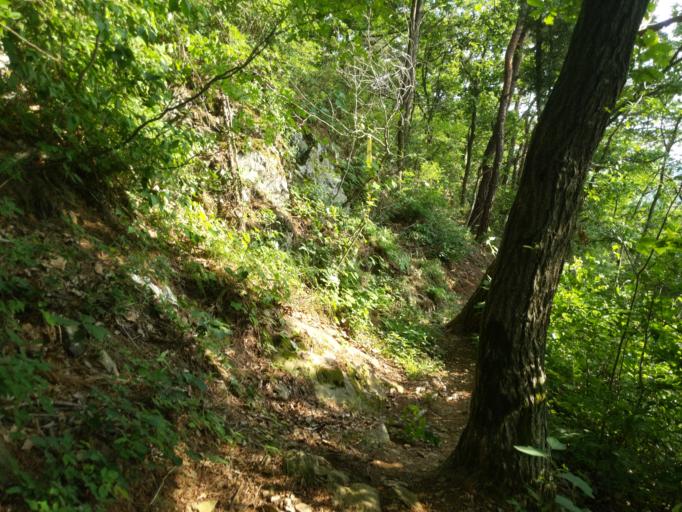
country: KR
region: Daegu
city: Hwawon
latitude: 35.7898
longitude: 128.5406
